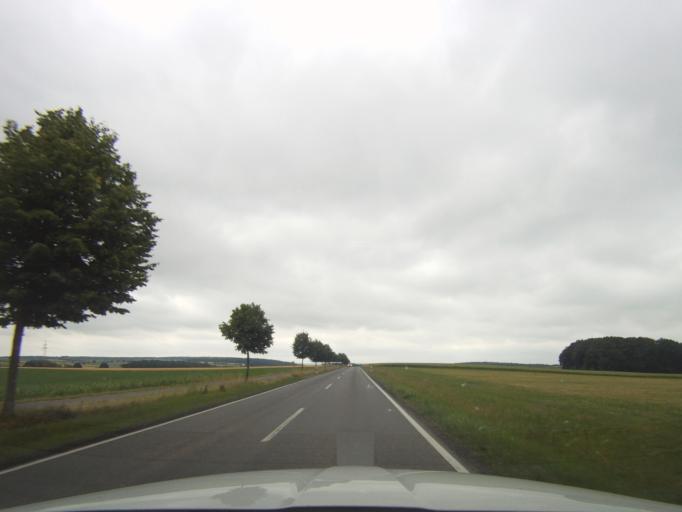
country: DE
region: Bavaria
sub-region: Upper Franconia
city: Weitramsdorf
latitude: 50.2170
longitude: 10.8921
